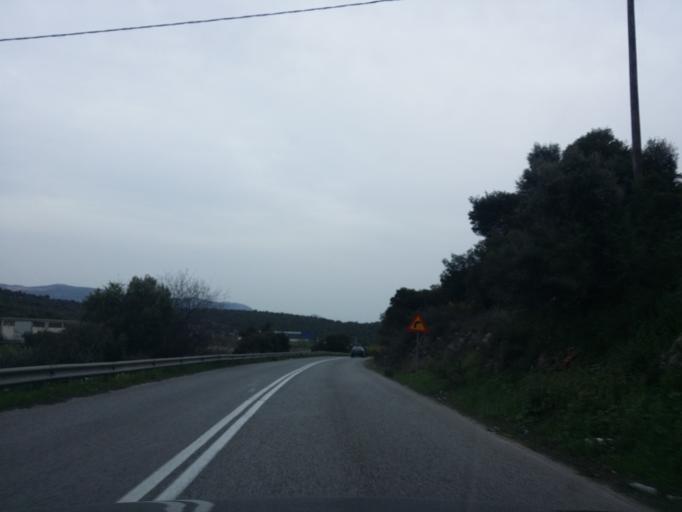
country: GR
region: Attica
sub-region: Nomarchia Dytikis Attikis
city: Mandra
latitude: 38.0846
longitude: 23.4881
